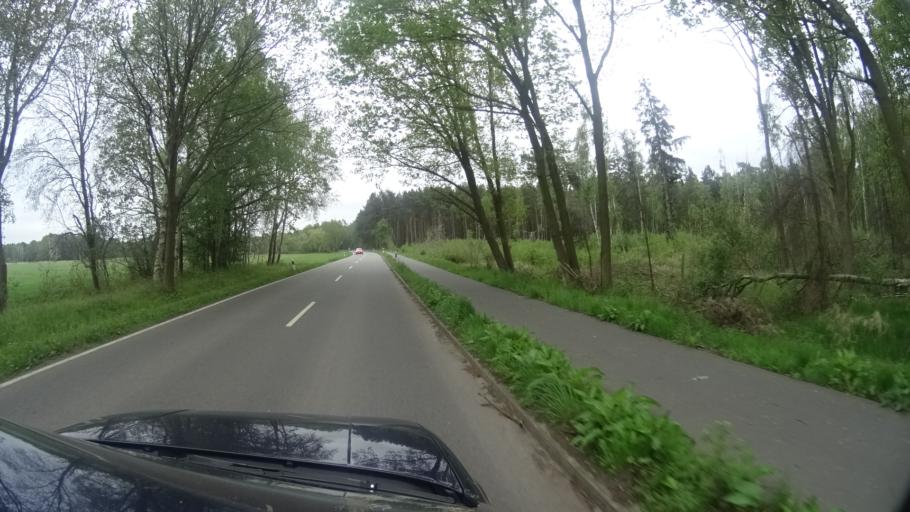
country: DE
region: Mecklenburg-Vorpommern
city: Ostseebad Dierhagen
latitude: 54.2769
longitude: 12.3244
